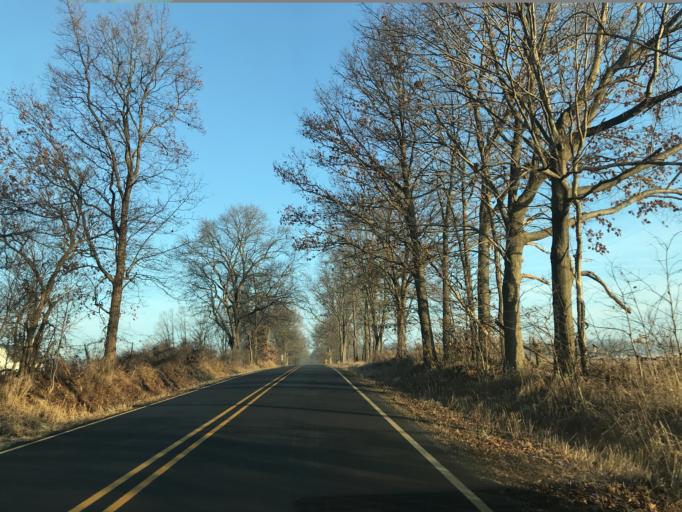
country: US
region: Michigan
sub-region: Ingham County
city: Leslie
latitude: 42.4228
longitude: -84.5263
